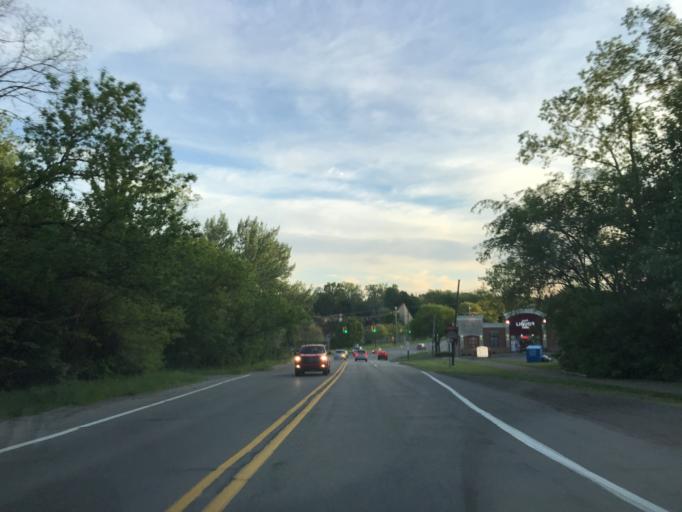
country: US
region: Michigan
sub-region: Wayne County
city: Northville
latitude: 42.4381
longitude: -83.4909
